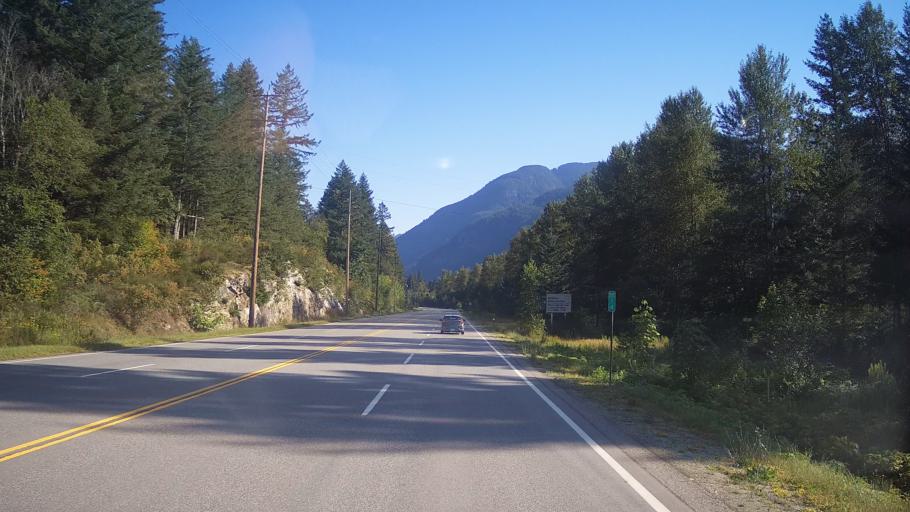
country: CA
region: British Columbia
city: Hope
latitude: 49.4818
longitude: -121.4227
